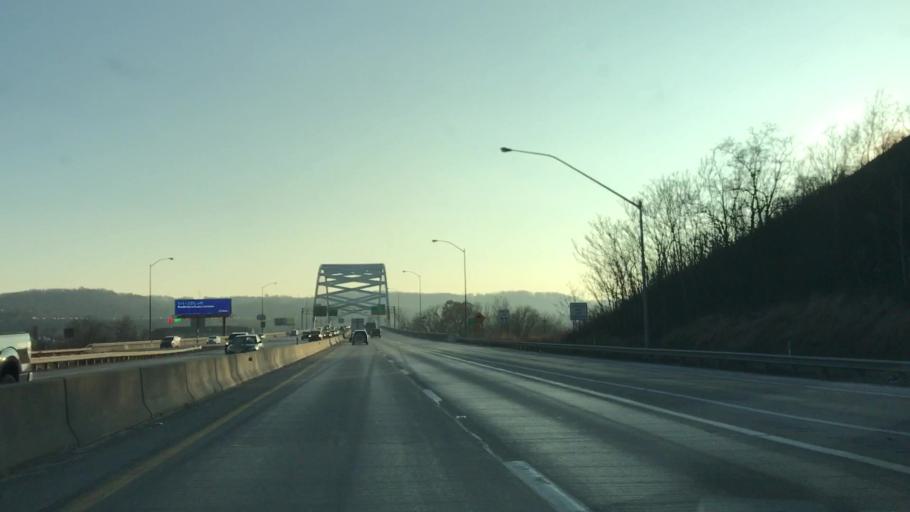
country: US
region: Pennsylvania
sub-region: Allegheny County
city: Coraopolis
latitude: 40.5196
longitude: -80.1324
